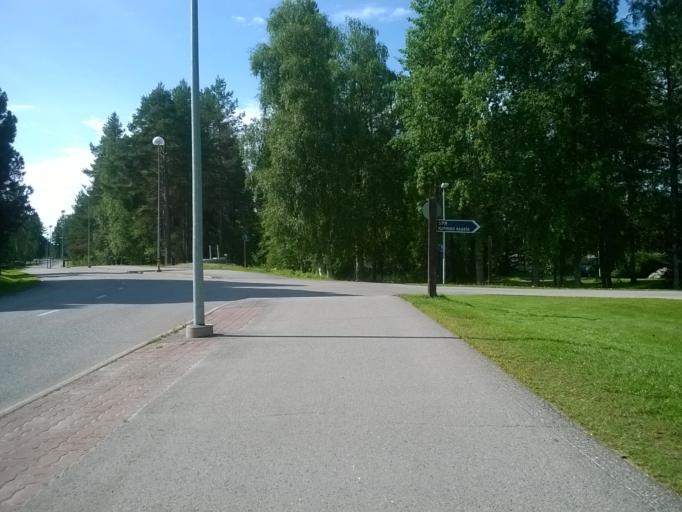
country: FI
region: Kainuu
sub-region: Kehys-Kainuu
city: Kuhmo
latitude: 64.1277
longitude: 29.5095
